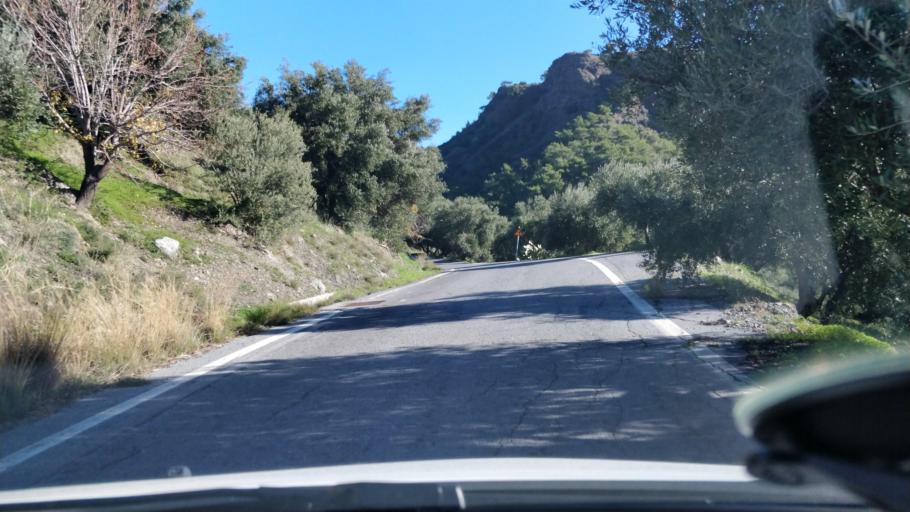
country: GR
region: Crete
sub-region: Nomos Lasithiou
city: Gra Liyia
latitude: 35.0507
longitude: 25.5810
